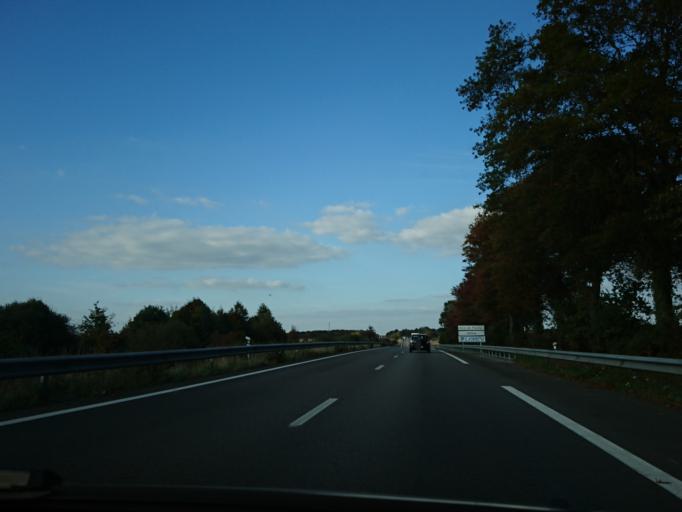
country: FR
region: Pays de la Loire
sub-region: Departement de la Loire-Atlantique
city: La Grigonnais
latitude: 47.5268
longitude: -1.6394
